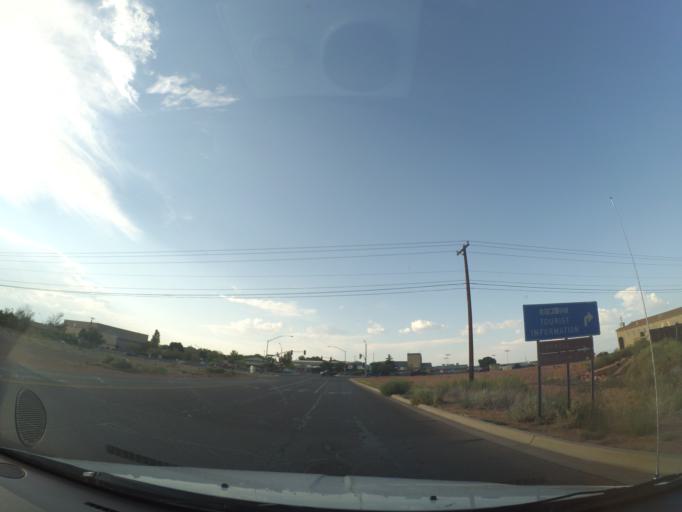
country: US
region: Arizona
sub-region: Coconino County
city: Page
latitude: 36.9101
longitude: -111.4556
